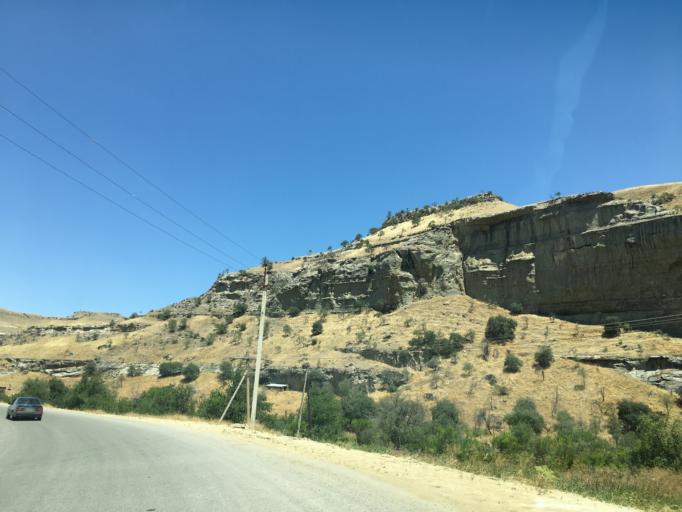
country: TM
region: Balkan
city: Magtymguly
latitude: 38.4170
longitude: 56.6799
